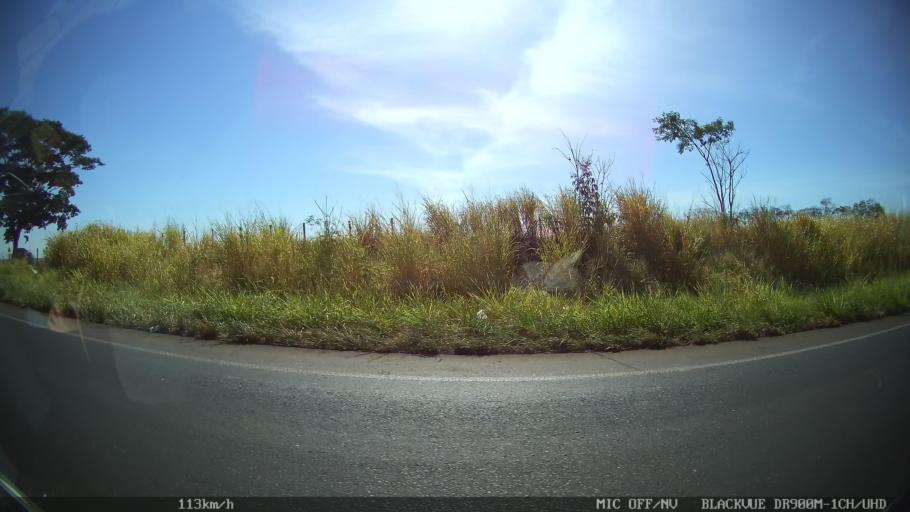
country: BR
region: Sao Paulo
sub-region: Olimpia
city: Olimpia
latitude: -20.6209
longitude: -48.7676
